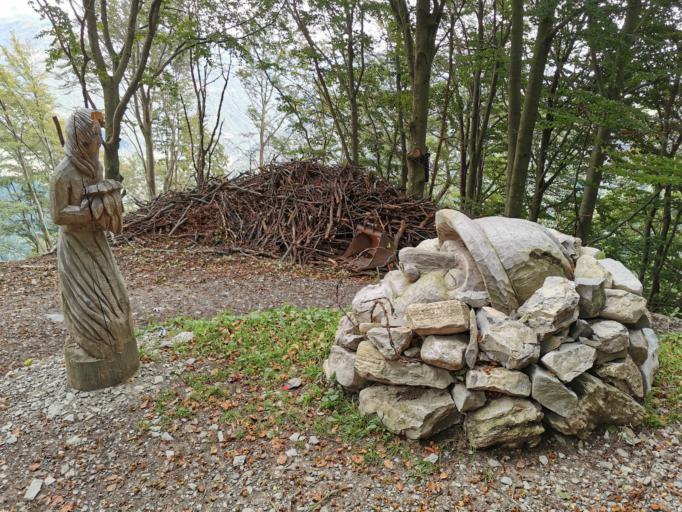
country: IT
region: Lombardy
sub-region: Provincia di Como
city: Occagno
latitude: 45.9125
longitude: 9.0866
